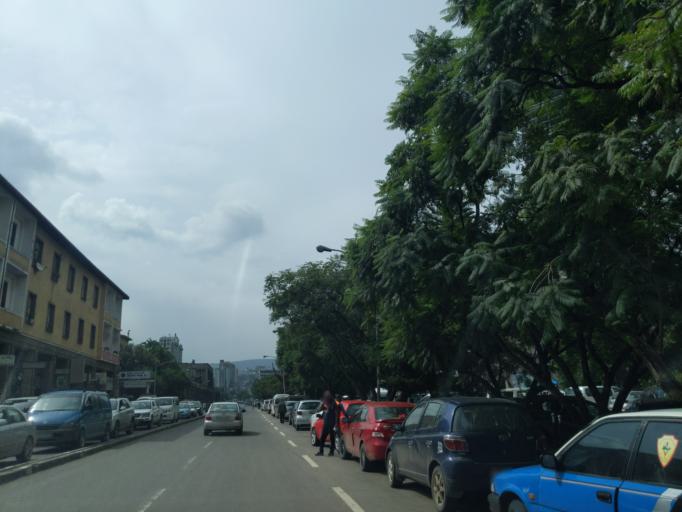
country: ET
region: Adis Abeba
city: Addis Ababa
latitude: 9.0142
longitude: 38.7529
